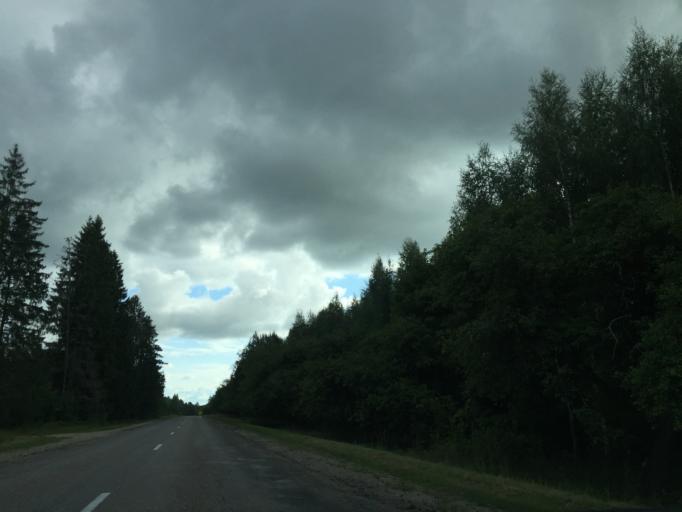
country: LV
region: Limbazu Rajons
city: Limbazi
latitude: 57.3614
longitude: 24.6702
